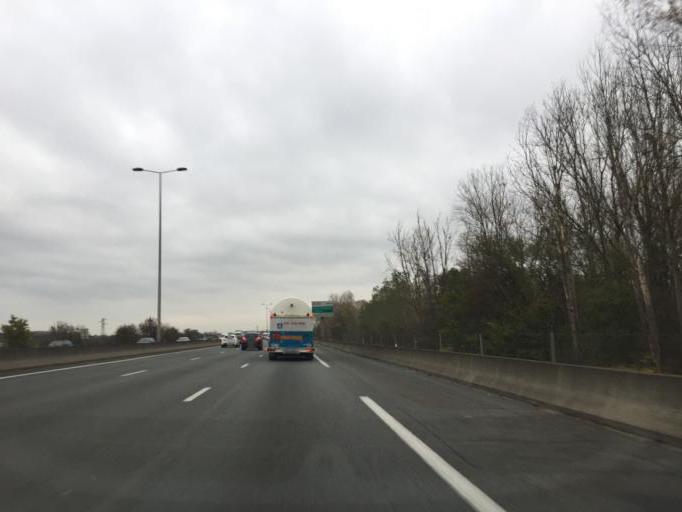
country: FR
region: Rhone-Alpes
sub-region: Departement du Rhone
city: Villefranche-sur-Saone
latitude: 45.9585
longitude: 4.7193
